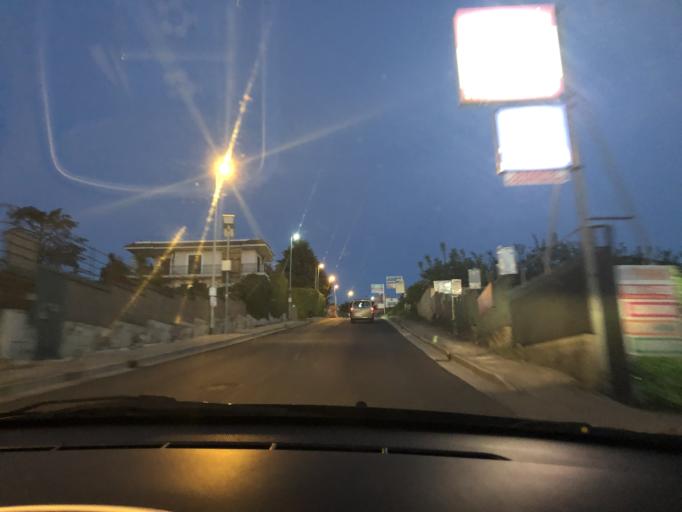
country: IT
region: Campania
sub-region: Provincia di Napoli
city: Torre Caracciolo
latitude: 40.8866
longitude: 14.1814
